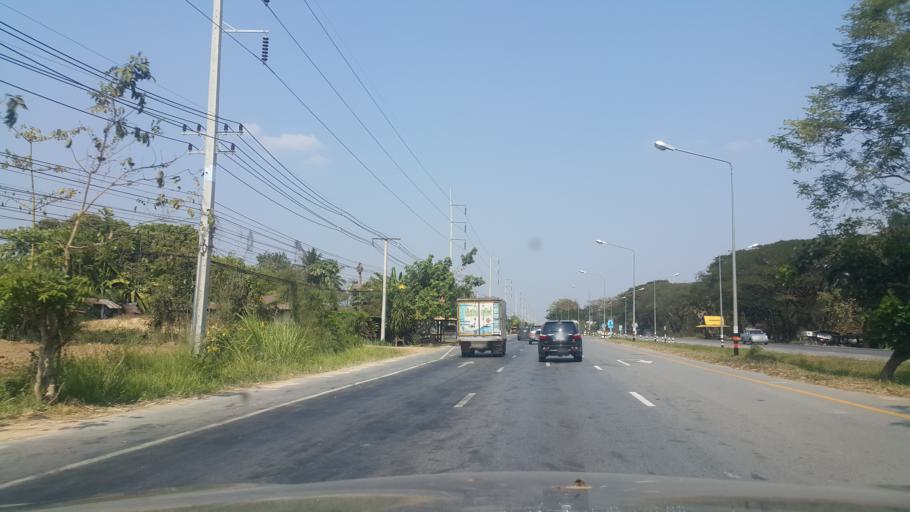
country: TH
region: Nakhon Ratchasima
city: Pak Thong Chai
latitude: 14.5731
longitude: 101.9840
